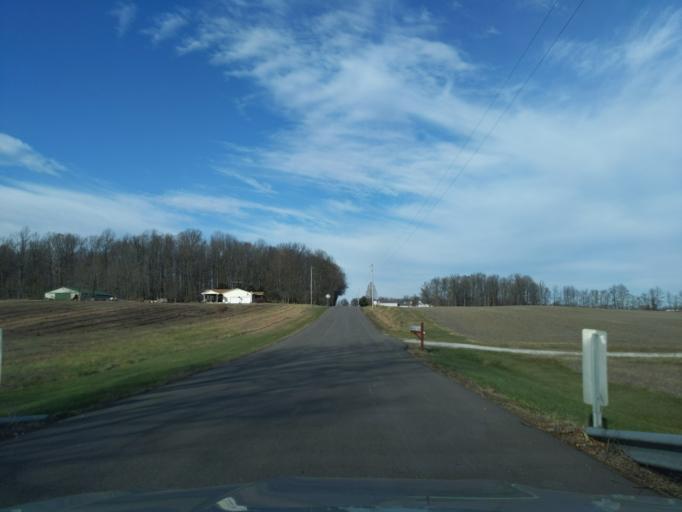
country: US
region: Indiana
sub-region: Decatur County
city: Greensburg
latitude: 39.2267
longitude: -85.4293
